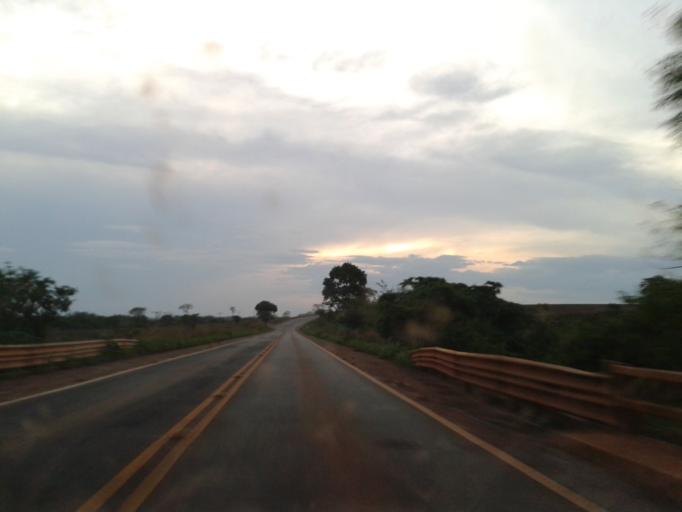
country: BR
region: Goias
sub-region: Santa Helena De Goias
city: Santa Helena de Goias
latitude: -17.8755
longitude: -50.7198
